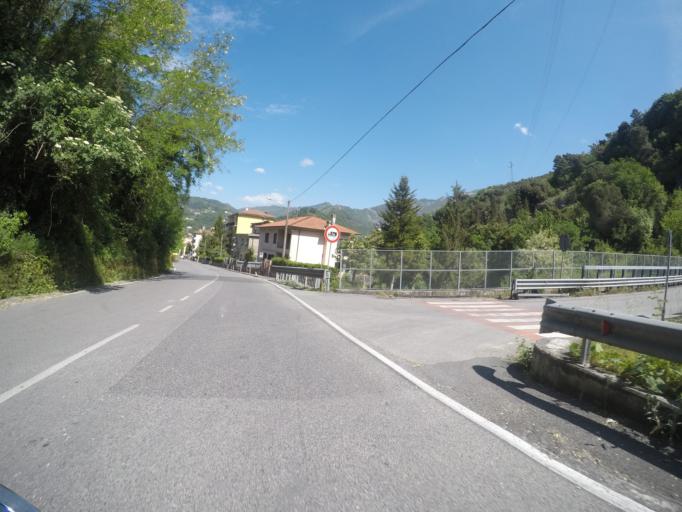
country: IT
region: Tuscany
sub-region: Provincia di Massa-Carrara
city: Carrara
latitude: 44.0739
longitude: 10.1062
